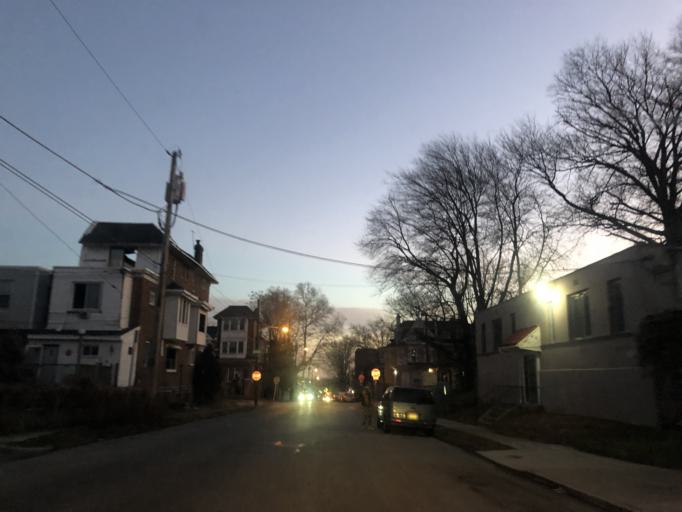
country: US
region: Pennsylvania
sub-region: Delaware County
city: Millbourne
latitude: 39.9806
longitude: -75.2428
